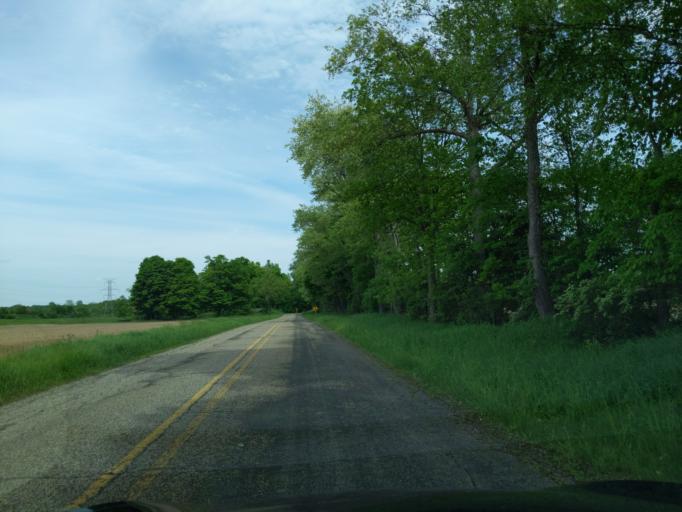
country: US
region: Michigan
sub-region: Ingham County
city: Leslie
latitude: 42.4168
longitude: -84.3370
